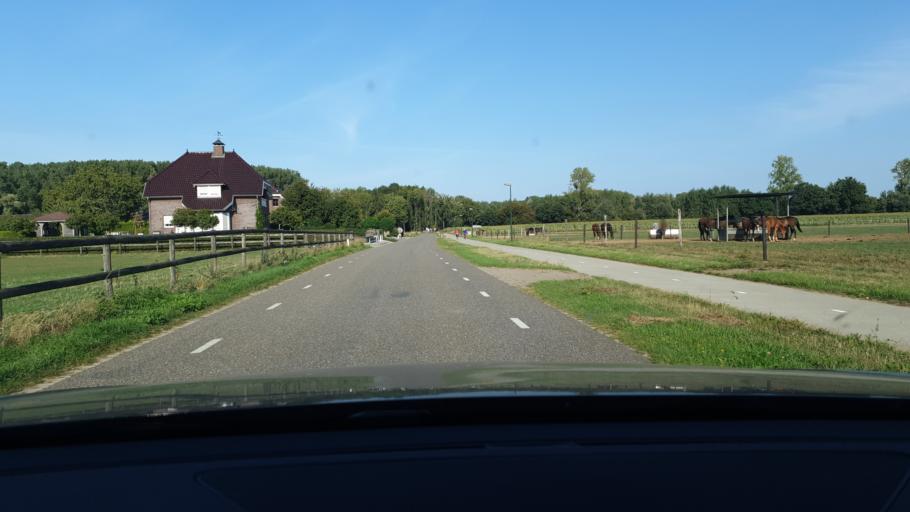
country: NL
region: Limburg
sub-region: Gemeente Maasgouw
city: Maasbracht
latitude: 51.0840
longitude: 5.8530
